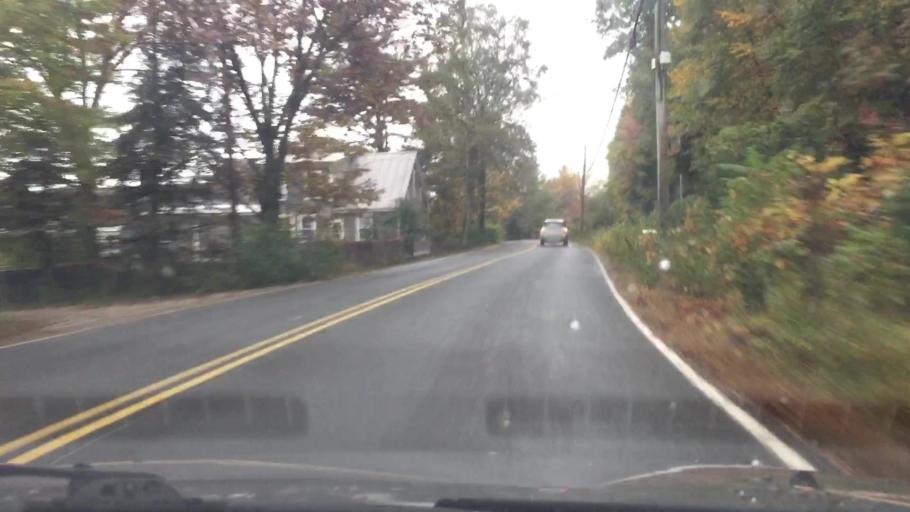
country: US
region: New Hampshire
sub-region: Cheshire County
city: Swanzey
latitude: 42.8954
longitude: -72.2836
